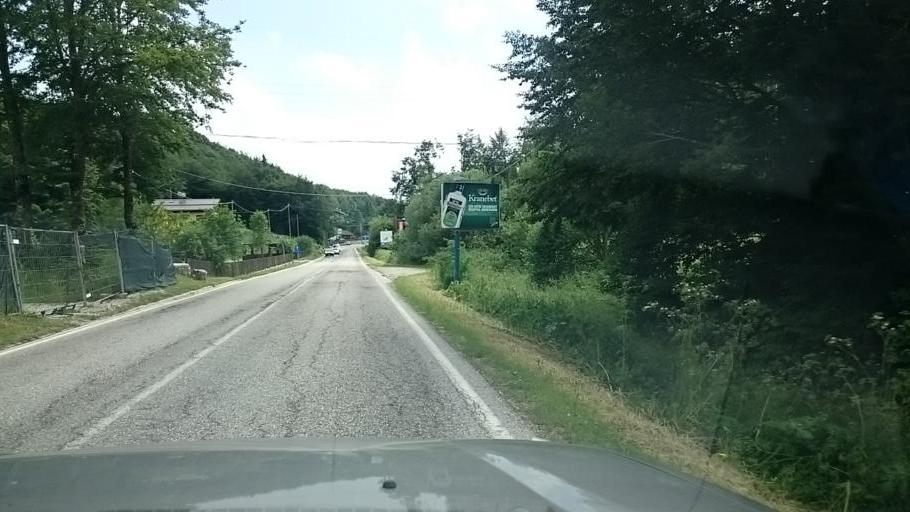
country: IT
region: Veneto
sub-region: Provincia di Vicenza
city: Conco
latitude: 45.8205
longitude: 11.6093
